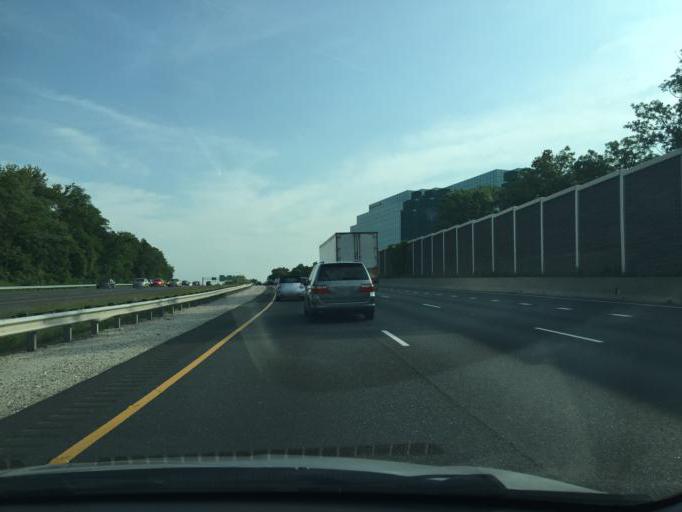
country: US
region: Maryland
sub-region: Baltimore County
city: Lutherville
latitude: 39.4318
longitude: -76.6341
